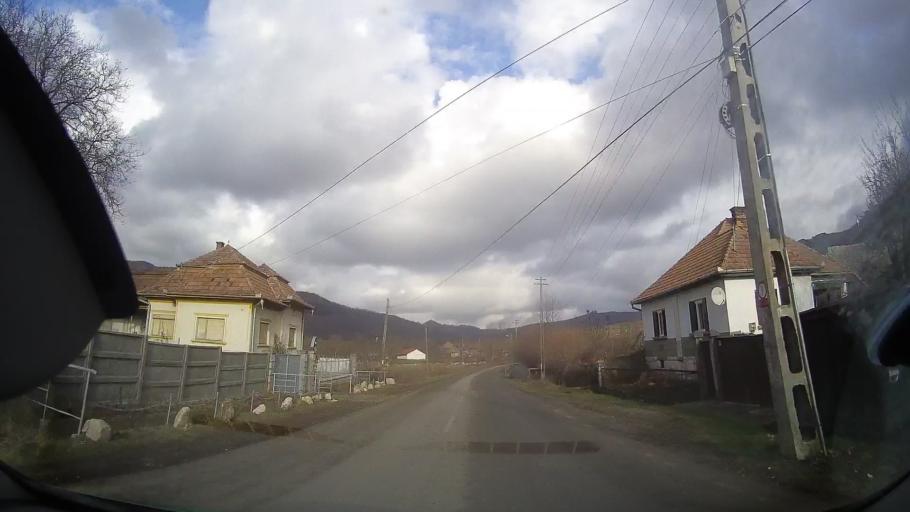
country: RO
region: Alba
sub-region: Comuna Rimetea
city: Rimetea
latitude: 46.4568
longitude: 23.5692
